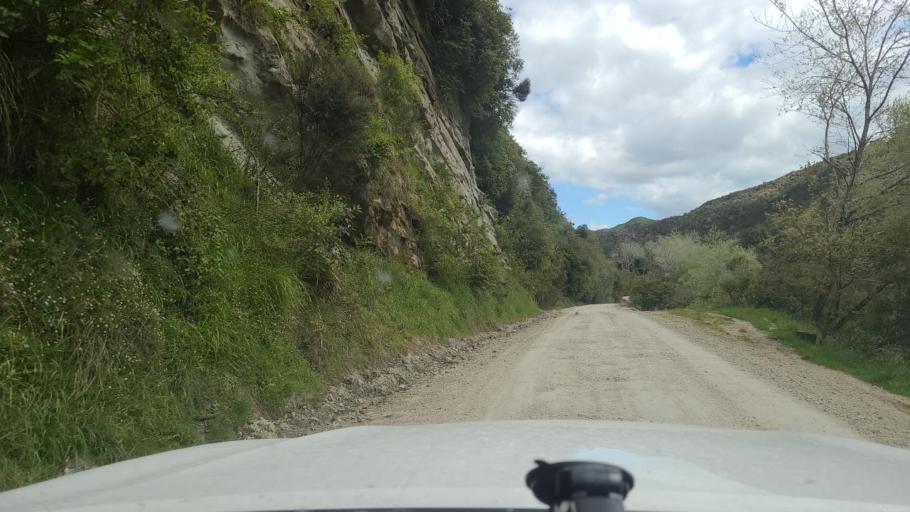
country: NZ
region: Gisborne
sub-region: Gisborne District
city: Gisborne
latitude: -38.8311
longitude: 177.7119
